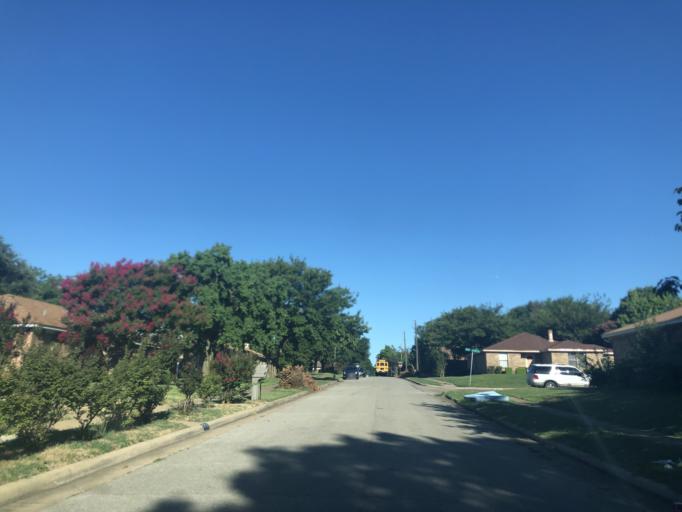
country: US
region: Texas
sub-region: Dallas County
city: Duncanville
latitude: 32.6447
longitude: -96.9442
